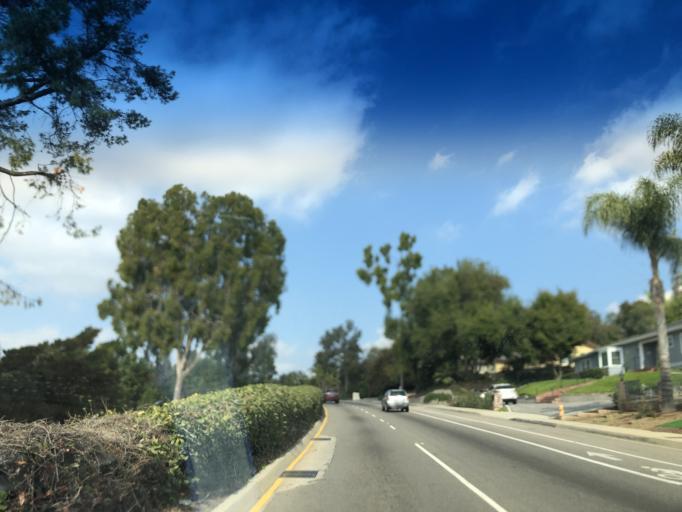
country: US
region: California
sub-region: Los Angeles County
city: East La Mirada
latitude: 33.9572
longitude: -118.0013
